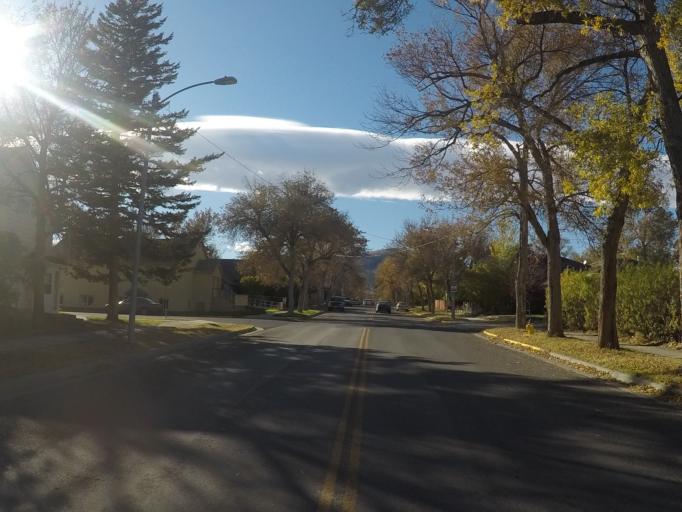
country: US
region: Montana
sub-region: Lewis and Clark County
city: Helena
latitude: 46.5867
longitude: -112.0238
